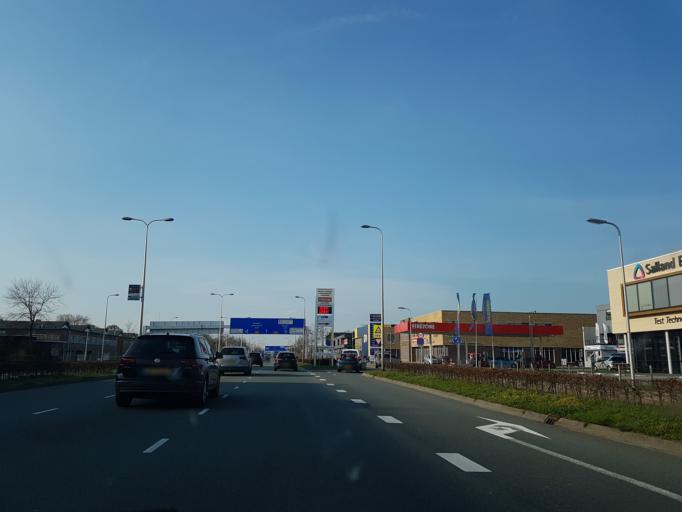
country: NL
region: Overijssel
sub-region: Gemeente Zwolle
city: Zwolle
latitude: 52.5196
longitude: 6.1185
